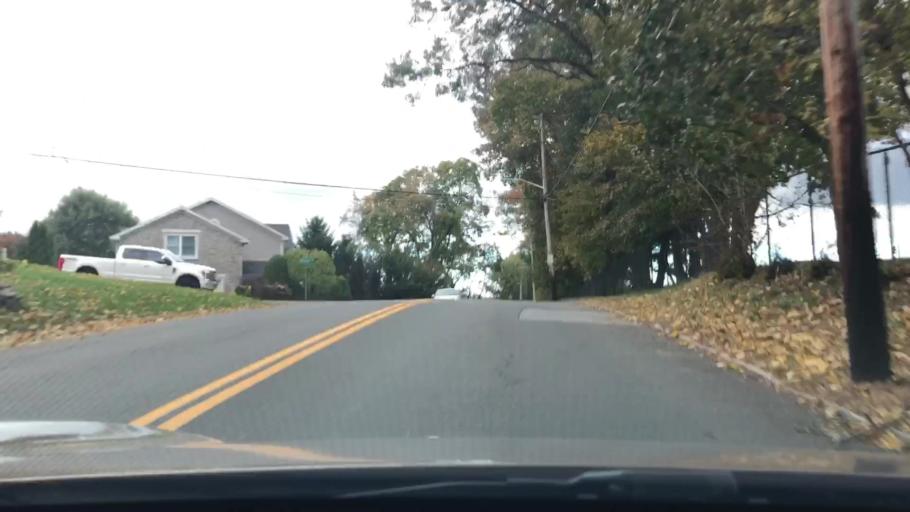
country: US
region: New York
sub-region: Westchester County
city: Tuckahoe
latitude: 40.9670
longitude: -73.8135
